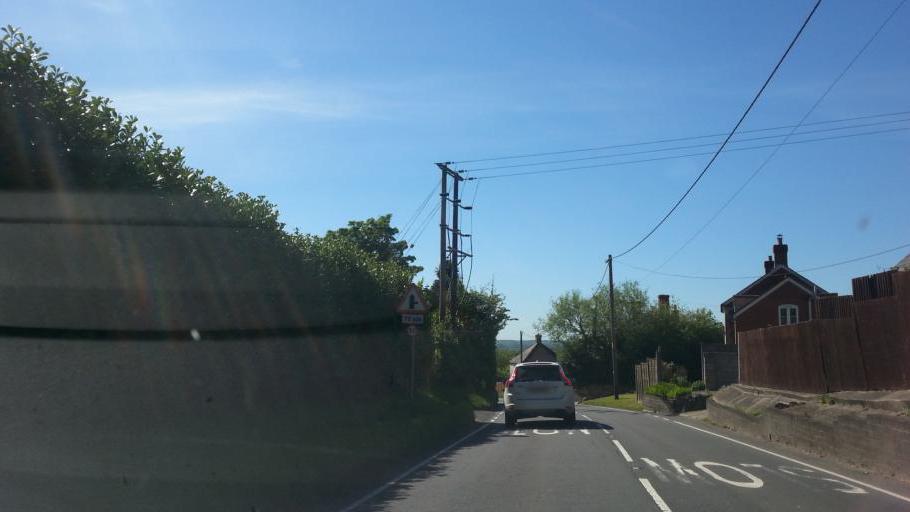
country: GB
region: England
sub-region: Dorset
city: Shaftesbury
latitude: 51.0087
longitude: -2.2117
